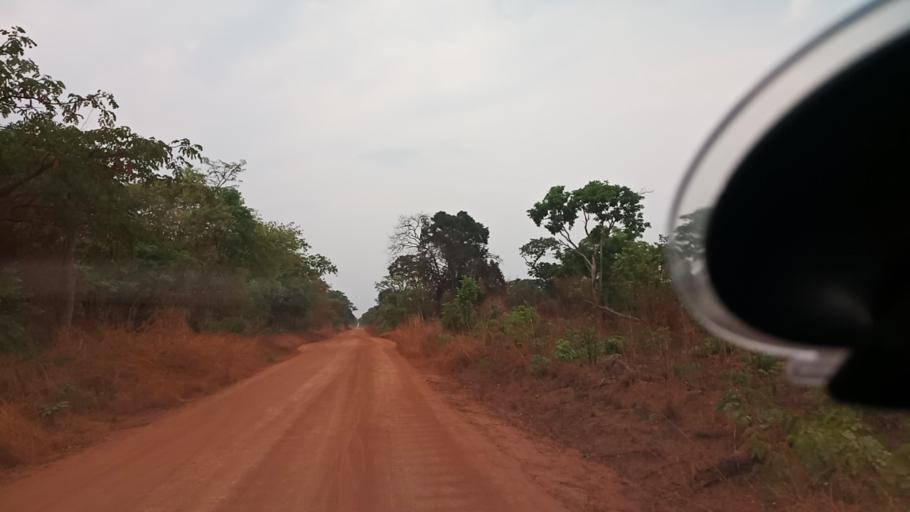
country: ZM
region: Luapula
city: Nchelenge
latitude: -9.4880
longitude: 28.2280
